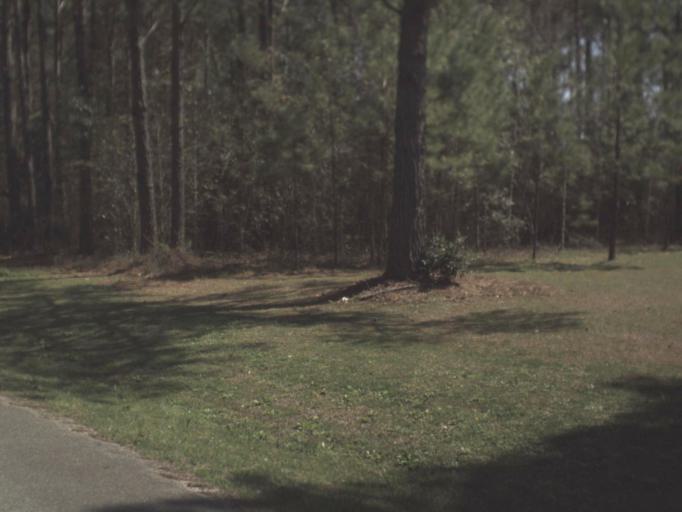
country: US
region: Florida
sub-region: Gadsden County
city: Gretna
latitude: 30.5925
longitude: -84.6735
